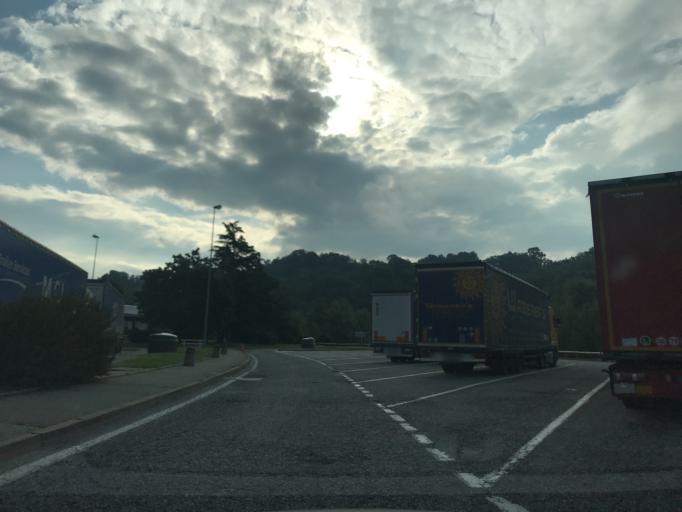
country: FR
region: Rhone-Alpes
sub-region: Departement de la Savoie
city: Coise-Saint-Jean-Pied-Gauthier
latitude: 45.5473
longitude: 6.1570
